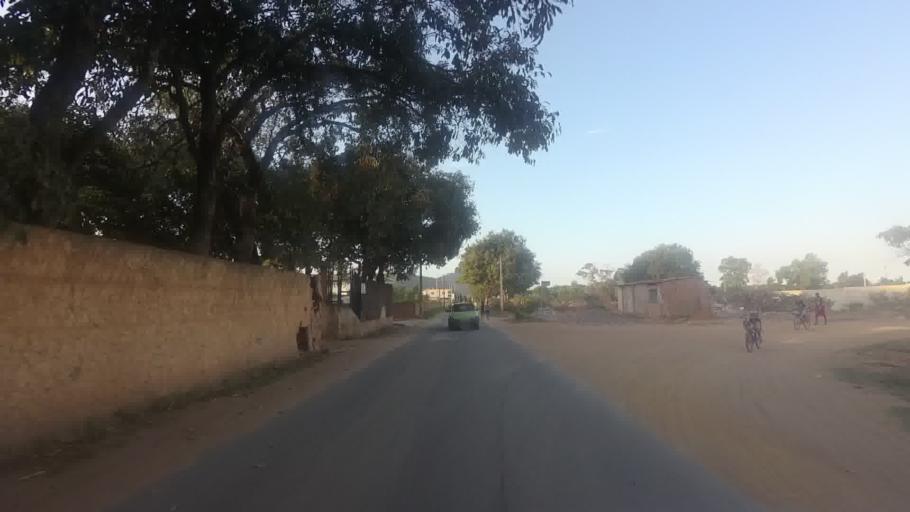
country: BR
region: Espirito Santo
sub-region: Piuma
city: Piuma
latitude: -20.8990
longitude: -40.7872
